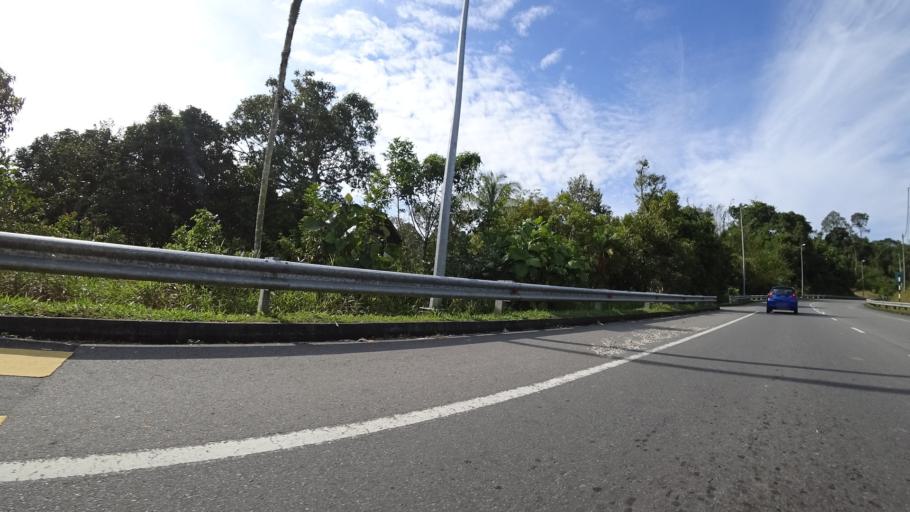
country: BN
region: Brunei and Muara
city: Bandar Seri Begawan
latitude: 4.8820
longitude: 114.8018
